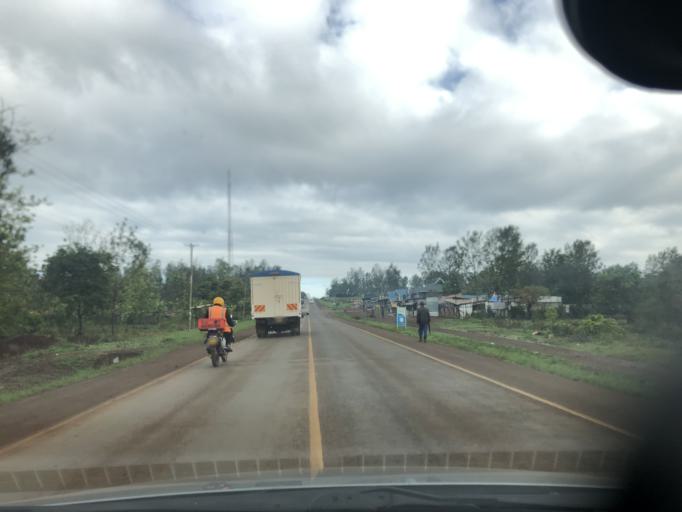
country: KE
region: Murang'a District
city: Maragua
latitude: -0.8377
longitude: 37.1380
